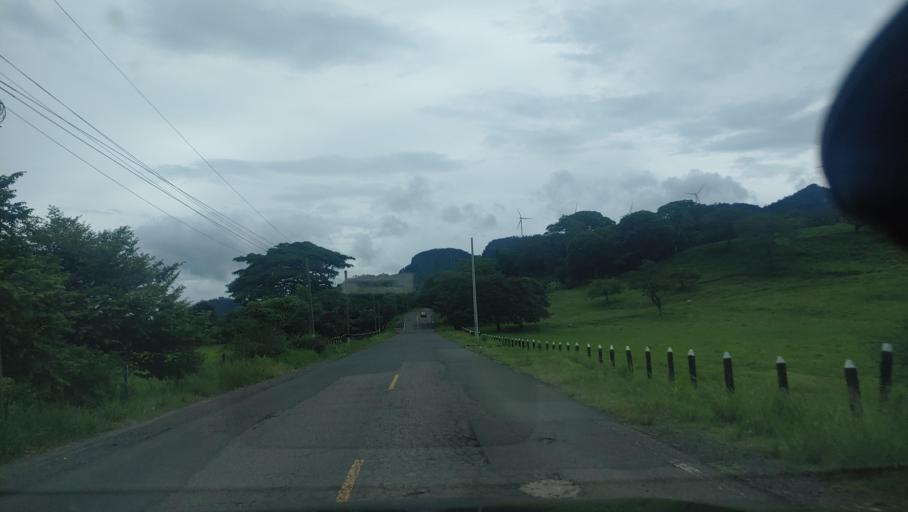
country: HN
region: Choluteca
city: Corpus
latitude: 13.3631
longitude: -86.9791
